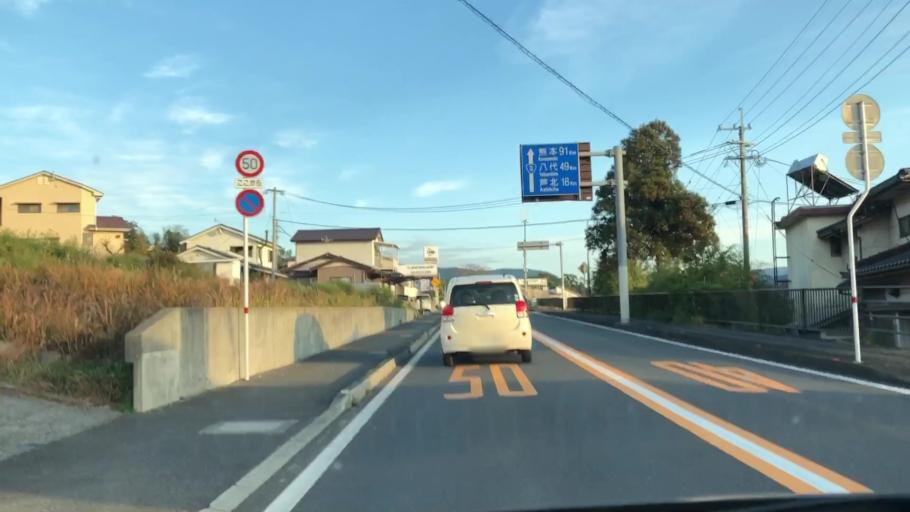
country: JP
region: Kumamoto
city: Minamata
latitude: 32.2110
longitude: 130.4110
